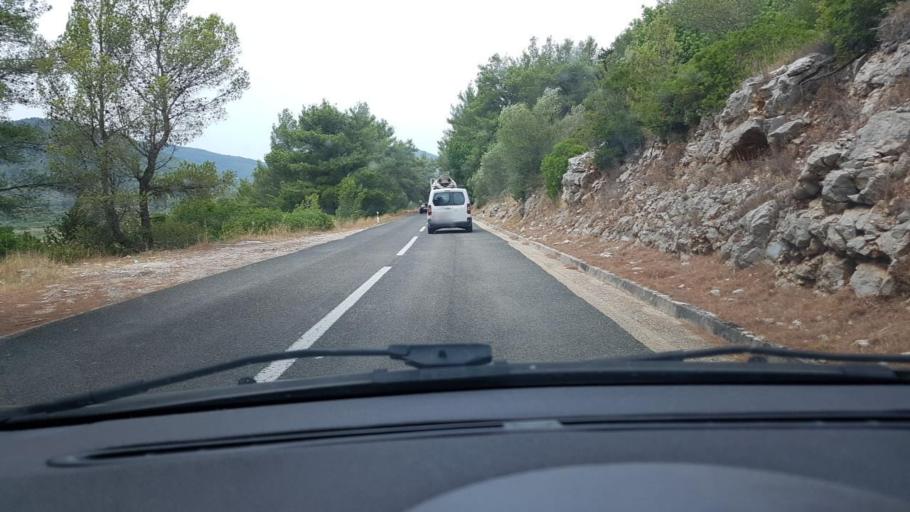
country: HR
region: Dubrovacko-Neretvanska
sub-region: Grad Dubrovnik
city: Vela Luka
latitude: 42.9505
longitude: 16.7889
